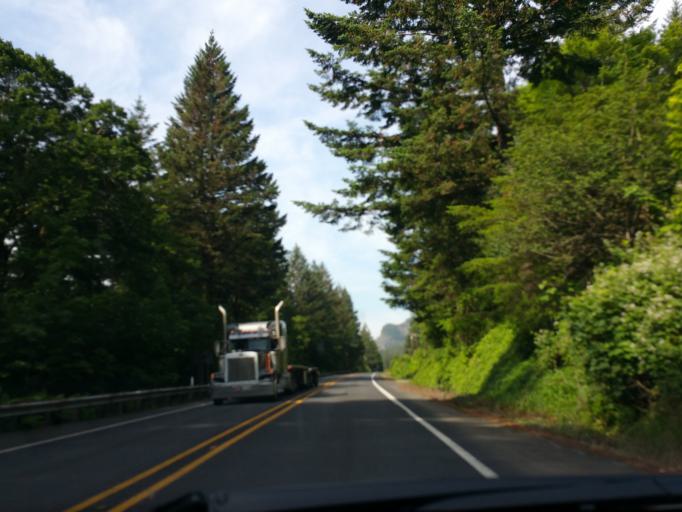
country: US
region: Oregon
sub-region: Hood River County
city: Cascade Locks
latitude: 45.6403
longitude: -121.9899
